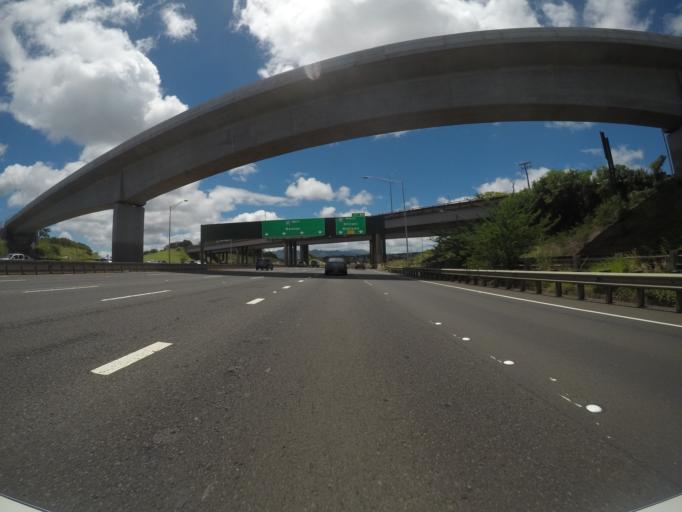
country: US
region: Hawaii
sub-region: Honolulu County
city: Pearl City, Manana
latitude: 21.3956
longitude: -157.9835
